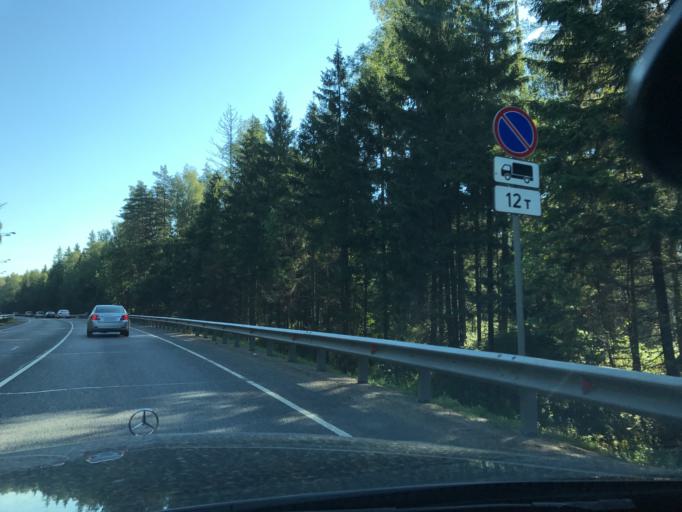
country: RU
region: Moskovskaya
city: Losino-Petrovskiy
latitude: 55.9306
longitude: 38.2079
